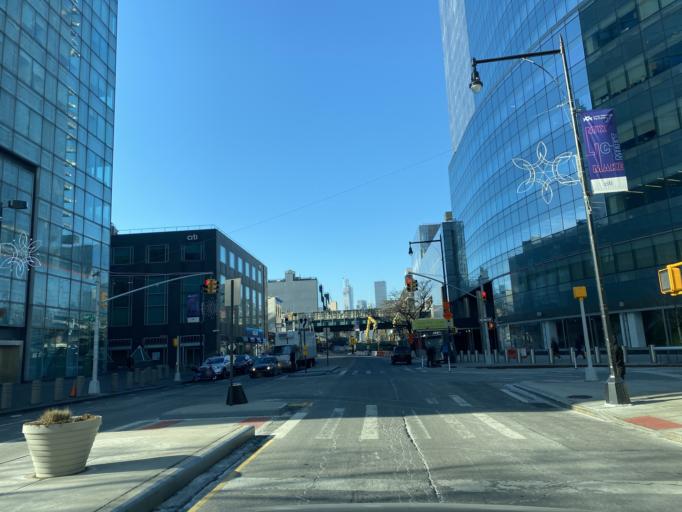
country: US
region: New York
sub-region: Queens County
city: Long Island City
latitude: 40.7474
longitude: -73.9435
